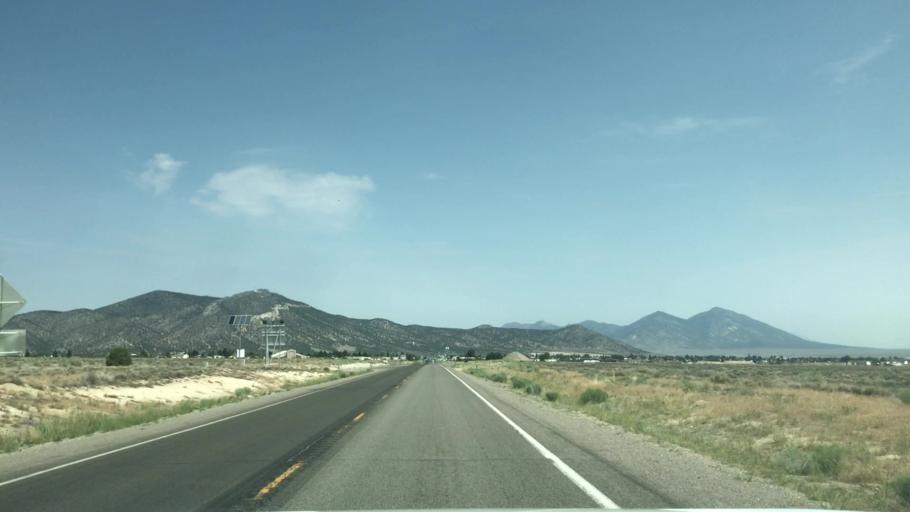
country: US
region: Nevada
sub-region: White Pine County
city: Ely
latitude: 39.2237
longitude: -114.8586
